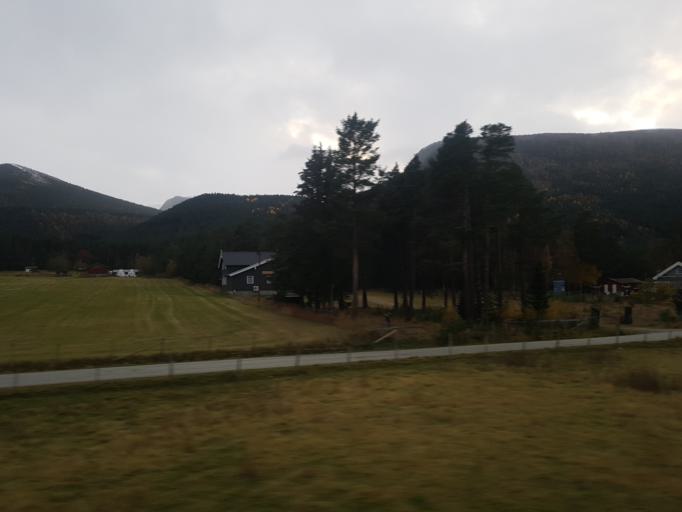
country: NO
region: Oppland
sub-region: Dovre
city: Dovre
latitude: 61.9721
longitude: 9.2588
